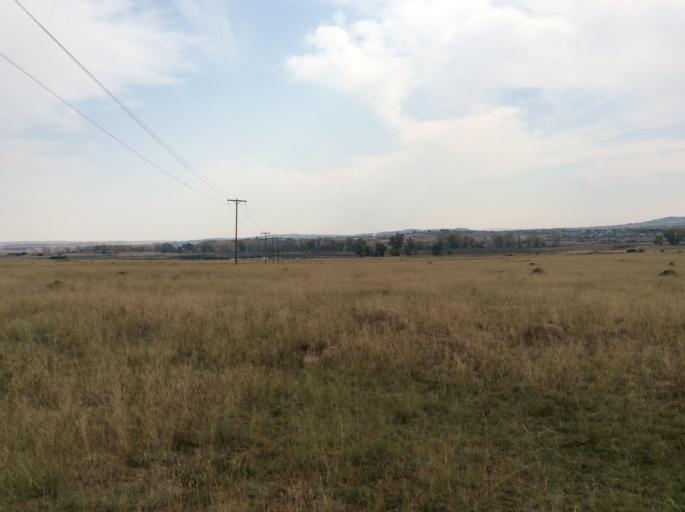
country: LS
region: Mafeteng
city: Mafeteng
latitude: -29.7329
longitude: 27.0242
